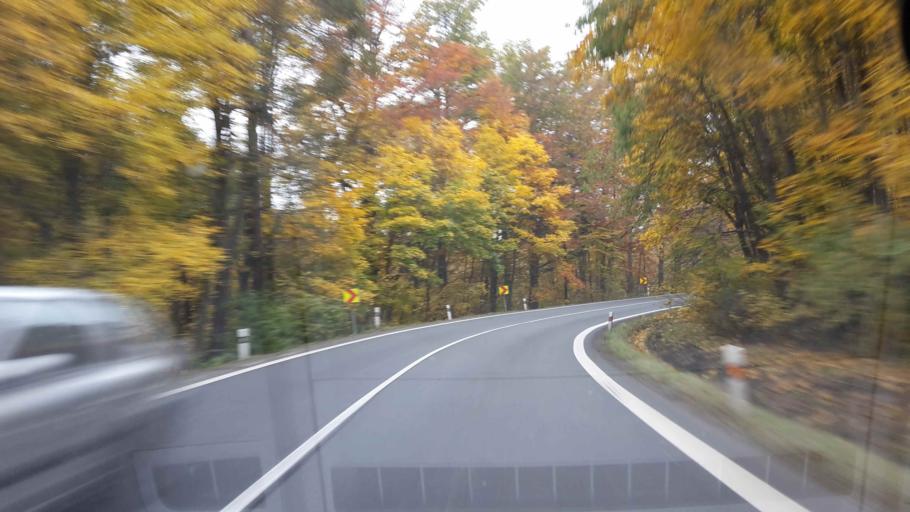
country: CZ
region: South Moravian
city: Damborice
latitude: 49.0828
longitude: 16.9318
